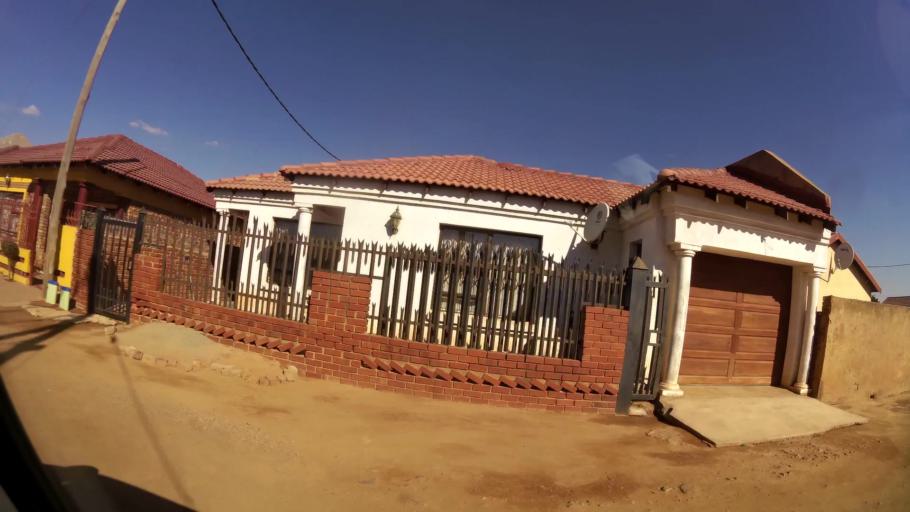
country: ZA
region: Gauteng
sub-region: City of Tshwane Metropolitan Municipality
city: Cullinan
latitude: -25.7134
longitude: 28.3920
